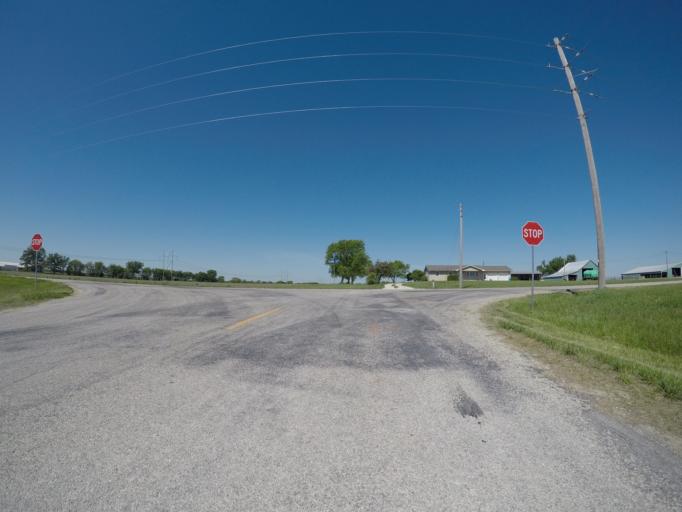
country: US
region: Kansas
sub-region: Osage County
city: Overbrook
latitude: 38.8405
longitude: -95.5560
